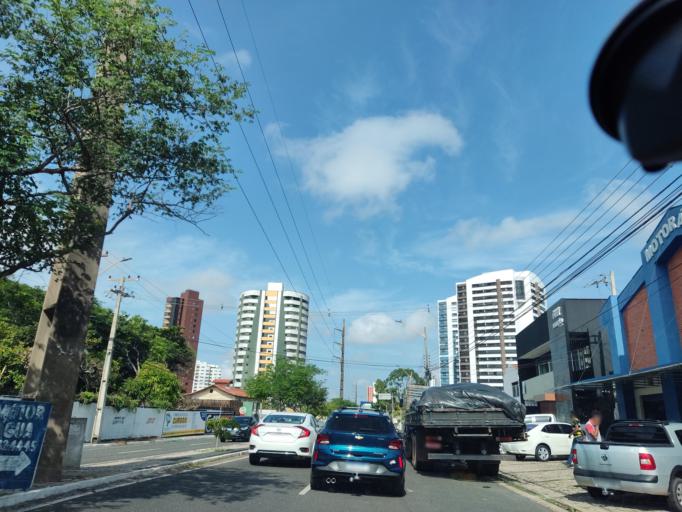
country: BR
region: Piaui
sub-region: Teresina
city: Teresina
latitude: -5.0702
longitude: -42.7753
